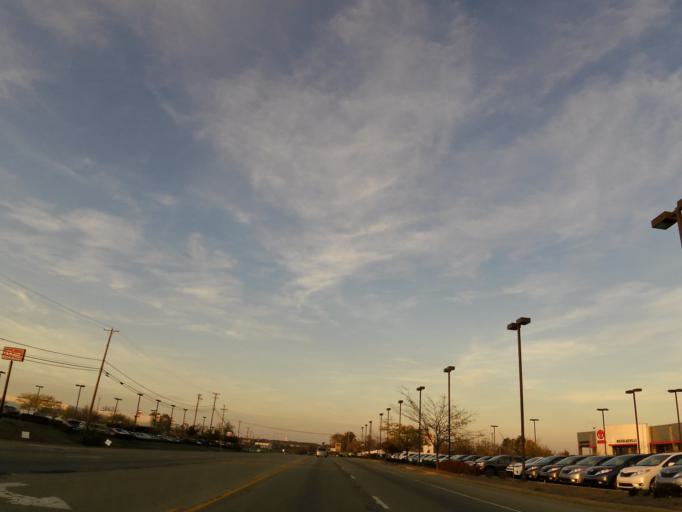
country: US
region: Kentucky
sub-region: Jessamine County
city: Nicholasville
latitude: 37.9165
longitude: -84.5572
